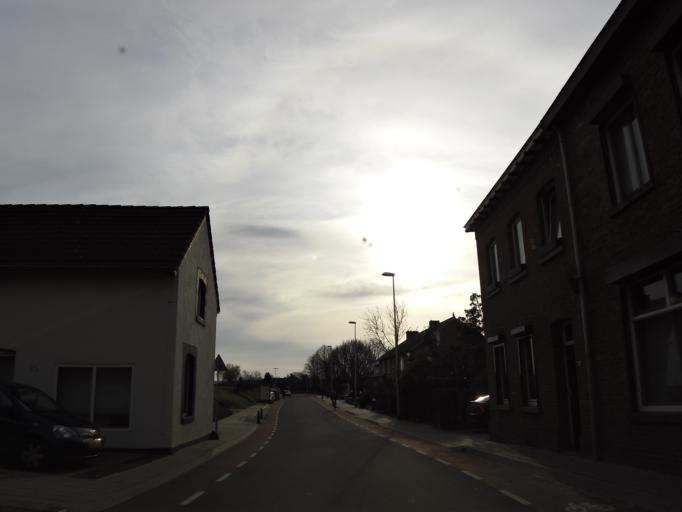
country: NL
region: Limburg
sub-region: Valkenburg aan de Geul
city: Schin op Geul
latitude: 50.8292
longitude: 5.8974
